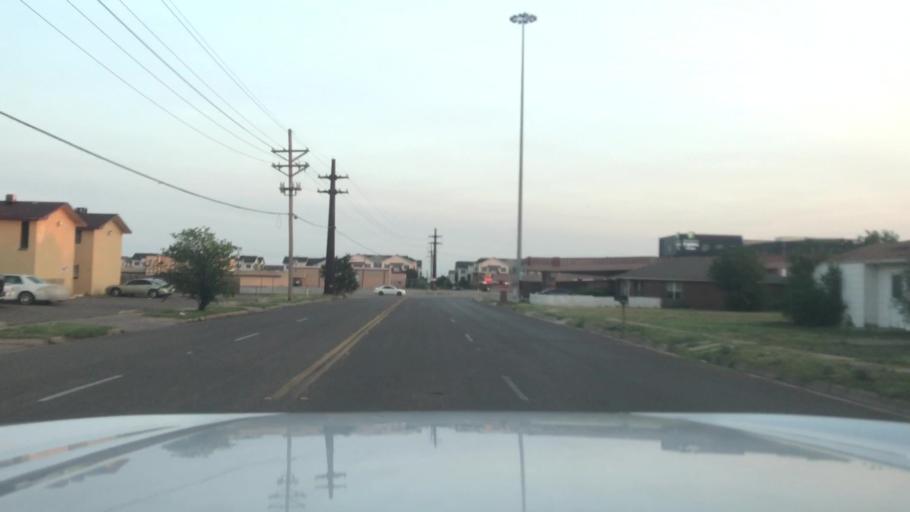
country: US
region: Texas
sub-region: Lubbock County
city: Lubbock
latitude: 33.5942
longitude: -101.8619
